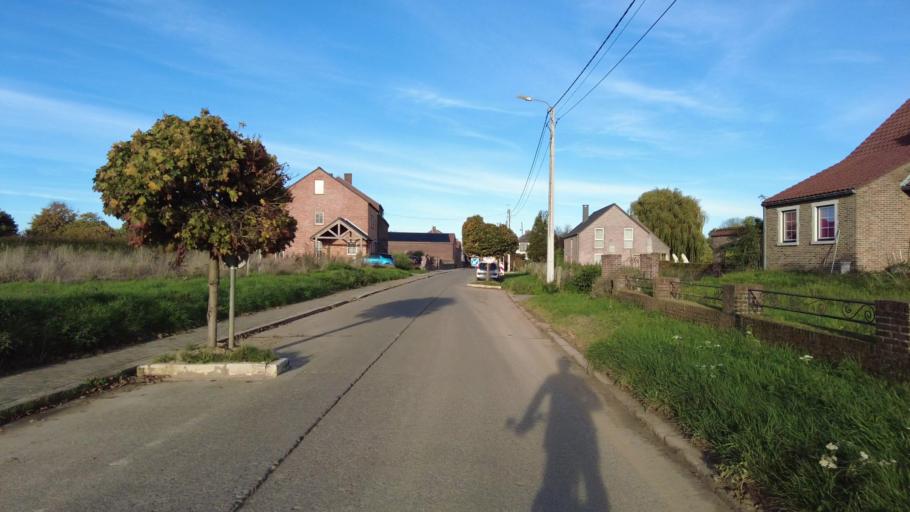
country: BE
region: Wallonia
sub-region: Province du Brabant Wallon
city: Jodoigne
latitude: 50.7140
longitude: 4.9229
